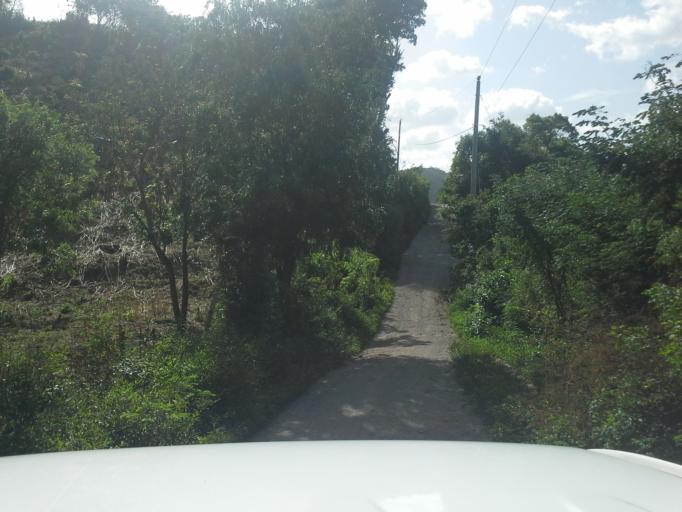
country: NI
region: Matagalpa
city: Ciudad Dario
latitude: 12.6689
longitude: -86.0476
